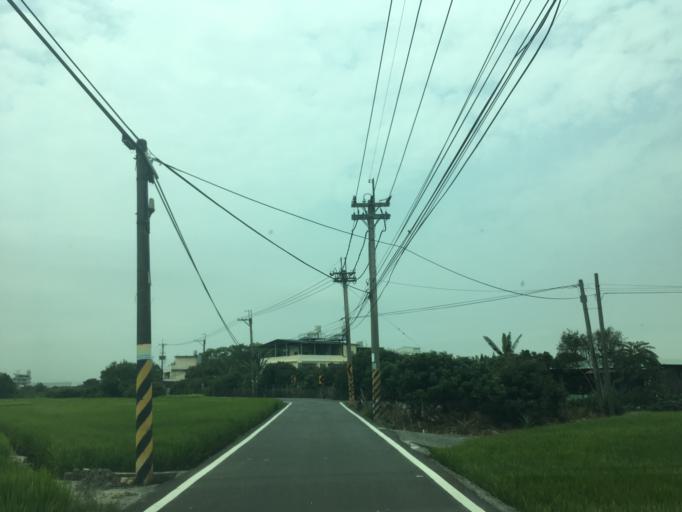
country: TW
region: Taiwan
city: Zhongxing New Village
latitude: 24.0389
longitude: 120.6866
